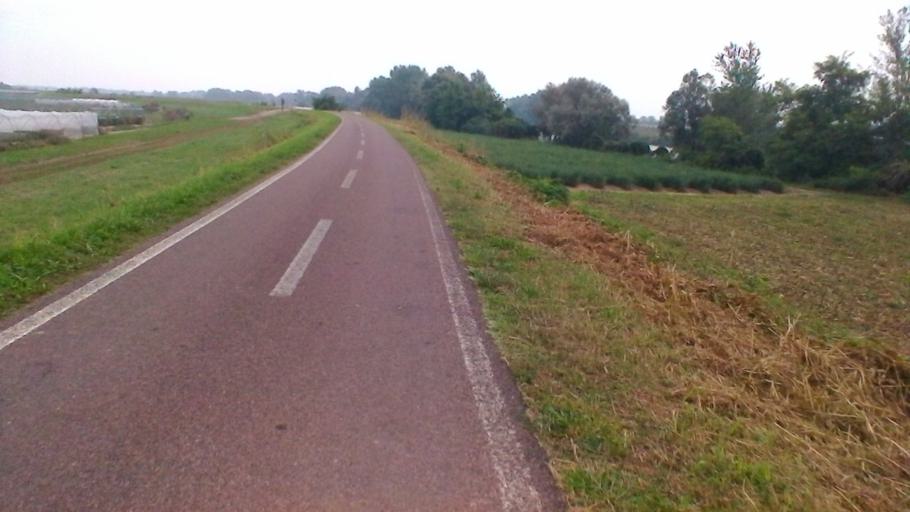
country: IT
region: Veneto
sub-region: Provincia di Verona
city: San Martino Buon Albergo
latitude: 45.3879
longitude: 11.0823
